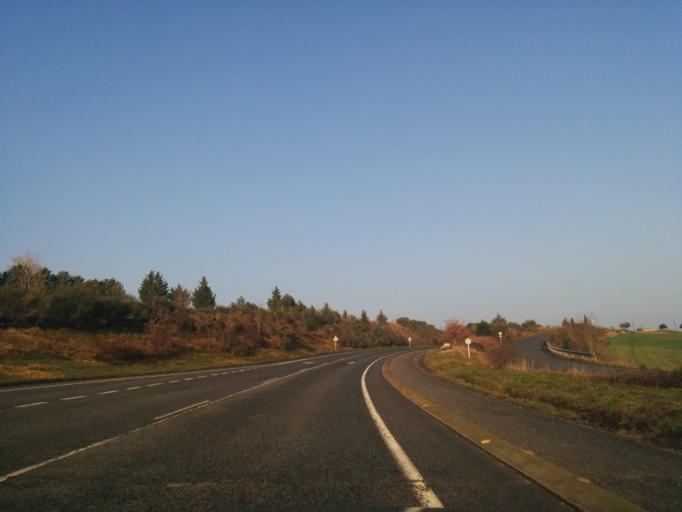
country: ES
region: Navarre
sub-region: Provincia de Navarra
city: Elorz
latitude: 42.7645
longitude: -1.5795
